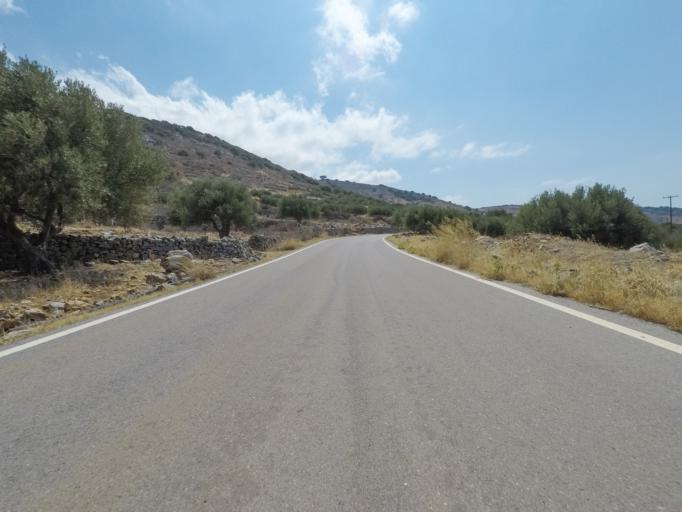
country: GR
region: Crete
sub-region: Nomos Lasithiou
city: Elounda
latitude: 35.3178
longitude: 25.6881
